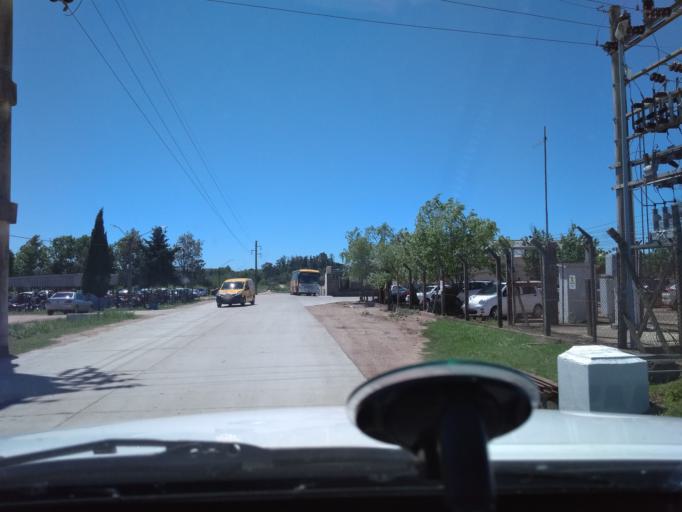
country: UY
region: Canelones
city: Progreso
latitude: -34.6873
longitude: -56.2971
